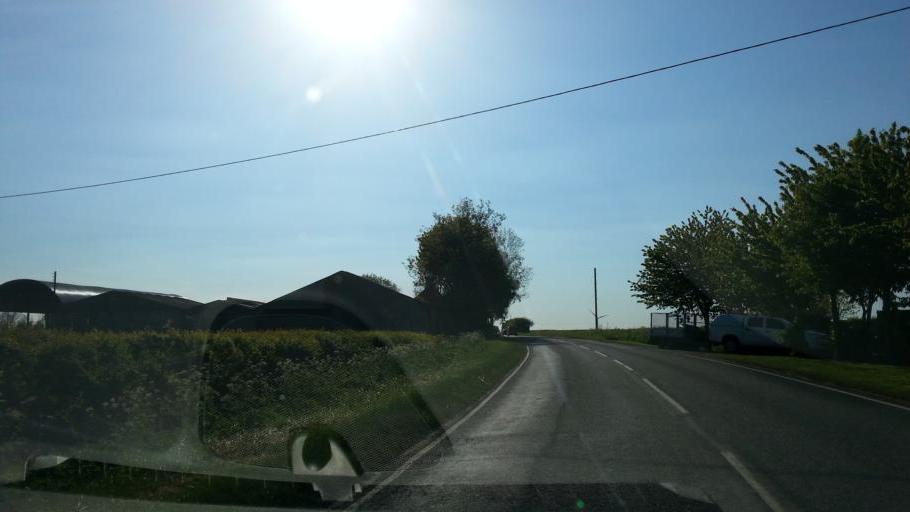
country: GB
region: England
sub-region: Lincolnshire
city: Long Bennington
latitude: 53.0375
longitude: -0.7618
